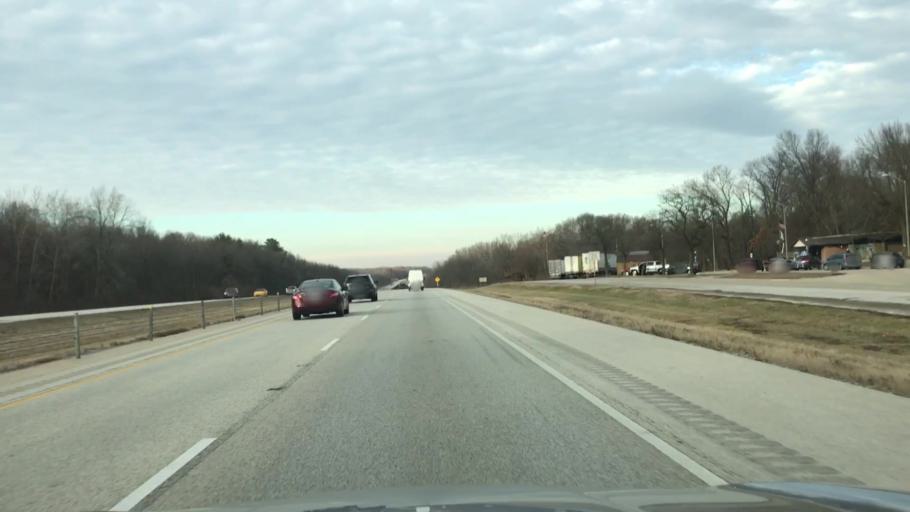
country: US
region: Illinois
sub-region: Sangamon County
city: Sherman
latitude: 39.8635
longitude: -89.5955
